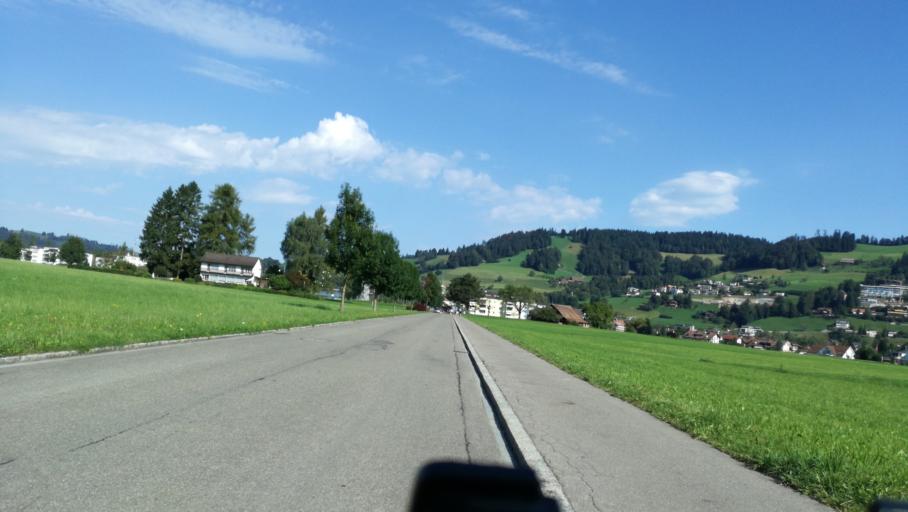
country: CH
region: Zug
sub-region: Zug
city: Unterageri
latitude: 47.1288
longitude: 8.5893
